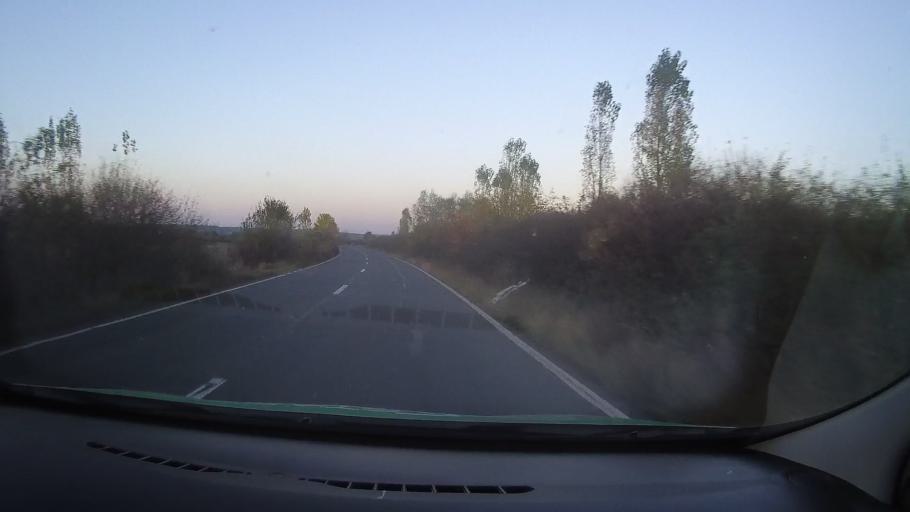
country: RO
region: Timis
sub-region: Comuna Dumbrava
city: Dumbrava
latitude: 45.8342
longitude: 22.1384
